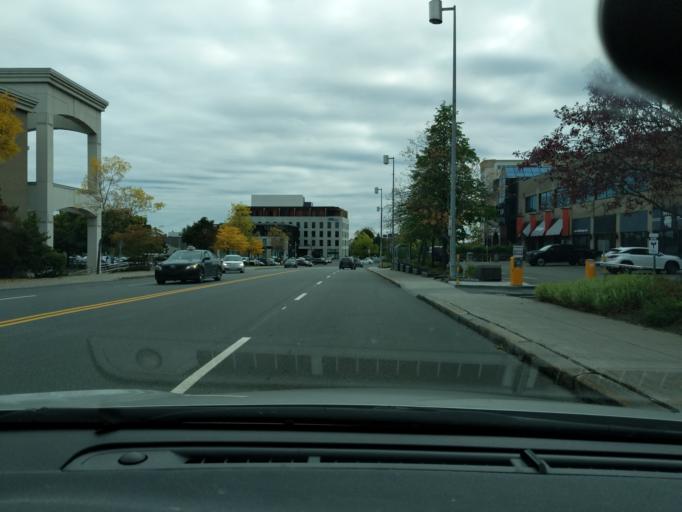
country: CA
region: Quebec
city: L'Ancienne-Lorette
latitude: 46.7693
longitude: -71.2877
